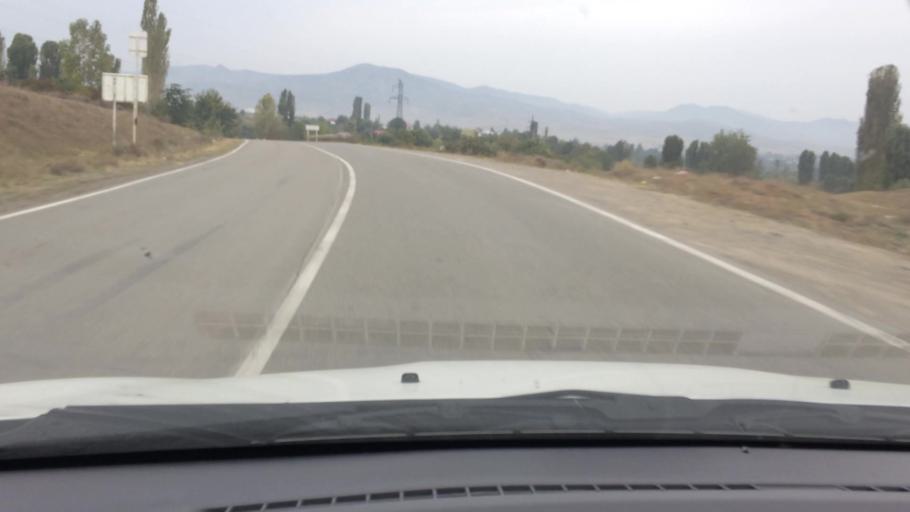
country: AM
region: Tavush
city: Bagratashen
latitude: 41.2332
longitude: 44.8151
